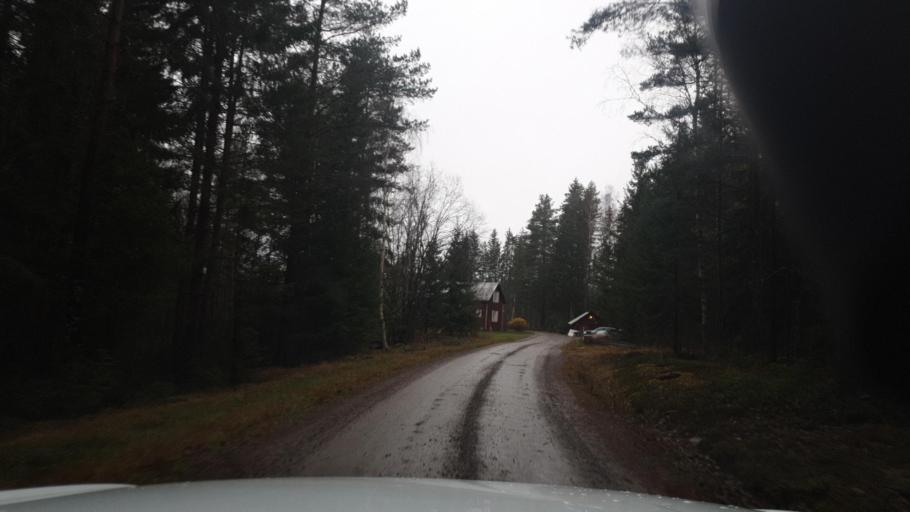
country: SE
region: Vaermland
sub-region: Arvika Kommun
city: Arvika
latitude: 59.5612
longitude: 12.8412
